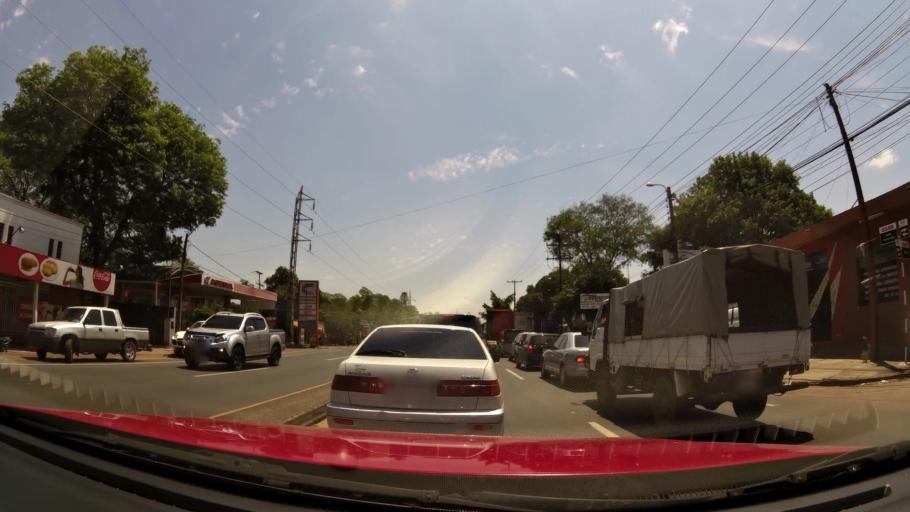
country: PY
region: Central
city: Villa Elisa
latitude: -25.3457
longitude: -57.5789
